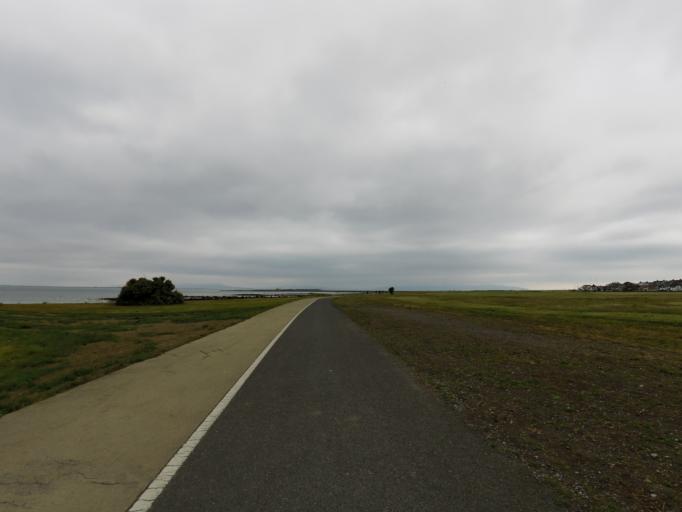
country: IE
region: Connaught
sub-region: County Galway
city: Gaillimh
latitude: 53.2666
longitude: -9.0502
